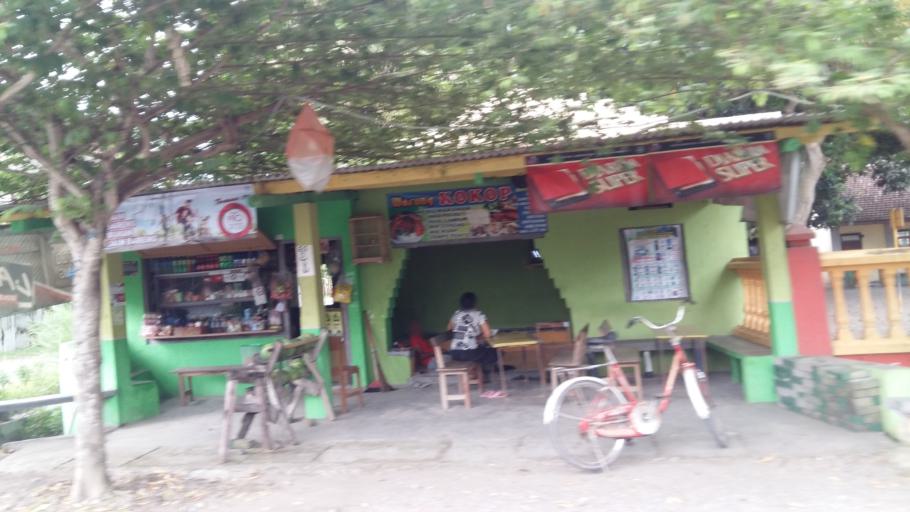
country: ID
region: East Java
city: Rejoagung Satu
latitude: -8.3365
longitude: 114.2986
